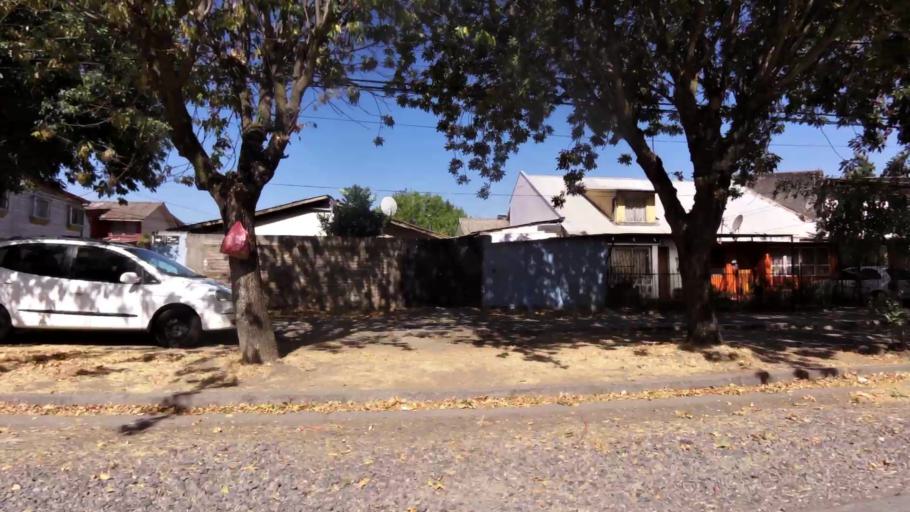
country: CL
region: Maule
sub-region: Provincia de Talca
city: Talca
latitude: -35.4350
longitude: -71.6606
